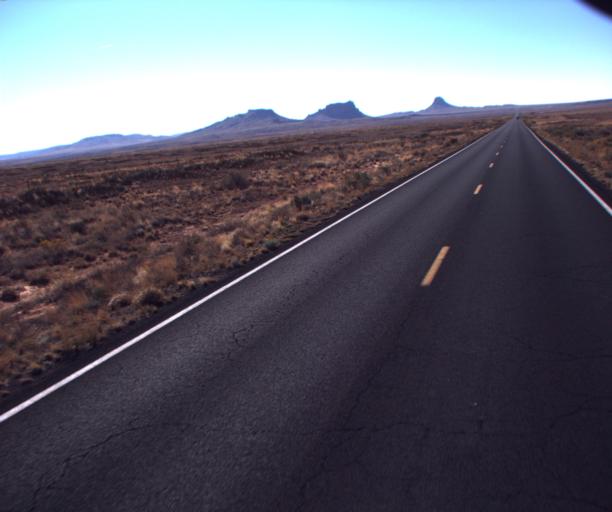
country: US
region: Arizona
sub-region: Navajo County
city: Dilkon
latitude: 35.3870
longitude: -110.4257
